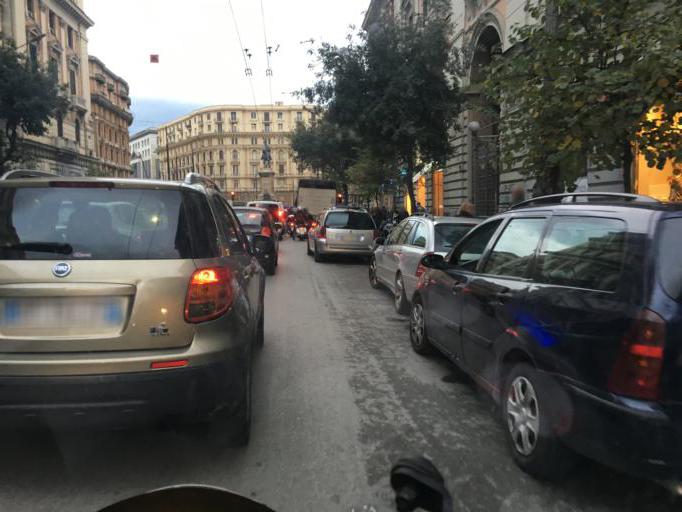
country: IT
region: Campania
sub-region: Provincia di Napoli
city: Napoli
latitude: 40.8448
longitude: 14.2580
